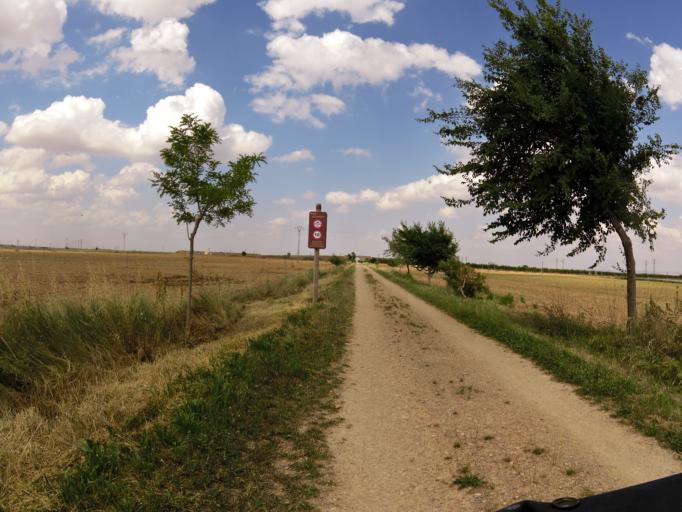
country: ES
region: Castille-La Mancha
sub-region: Provincia de Albacete
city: Albacete
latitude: 38.9275
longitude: -1.9977
